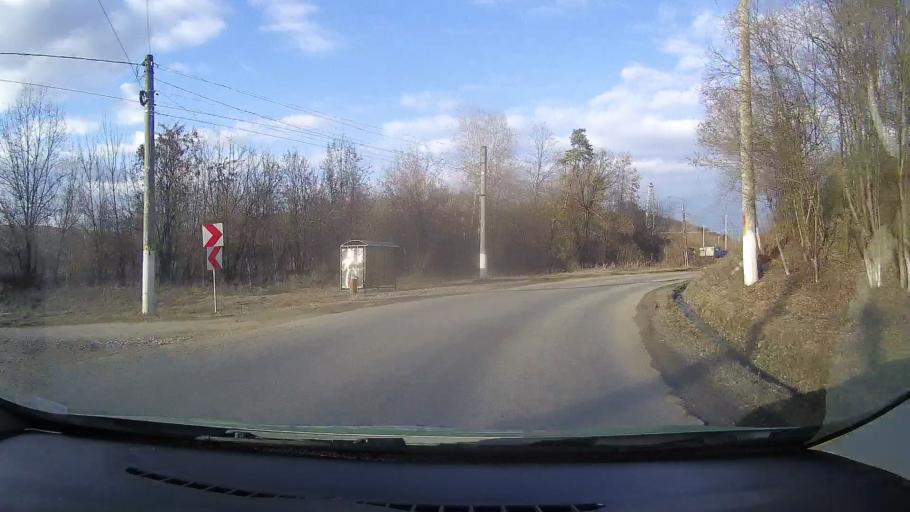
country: RO
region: Dambovita
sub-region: Comuna Ocnita
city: Ocnita
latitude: 44.9691
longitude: 25.5478
